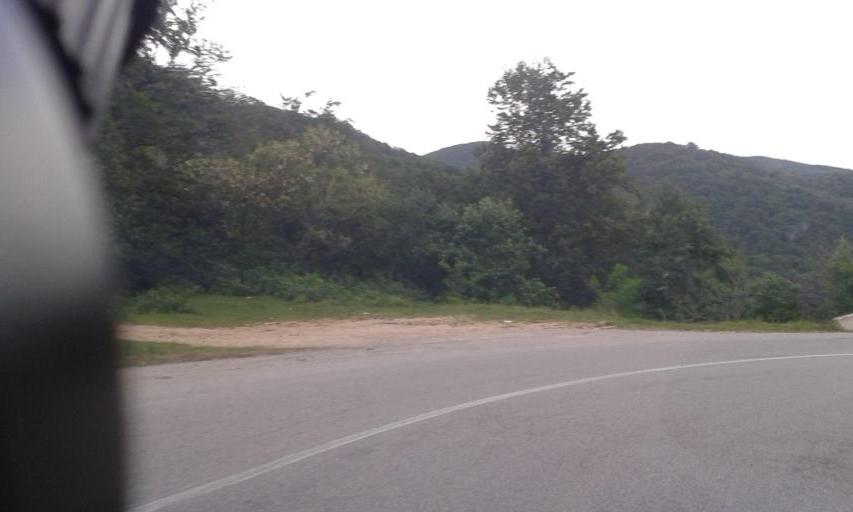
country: RO
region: Gorj
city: Novaci-Straini
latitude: 45.2280
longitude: 23.6937
